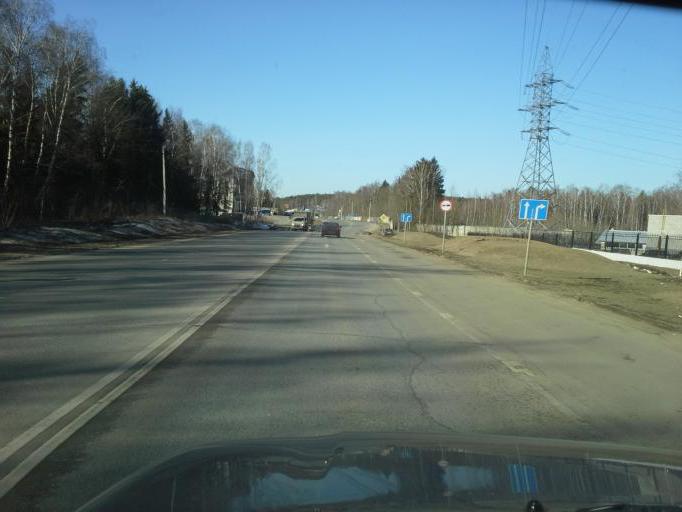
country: RU
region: Moskovskaya
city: Gorki Vtoryye
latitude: 55.6813
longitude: 37.1479
